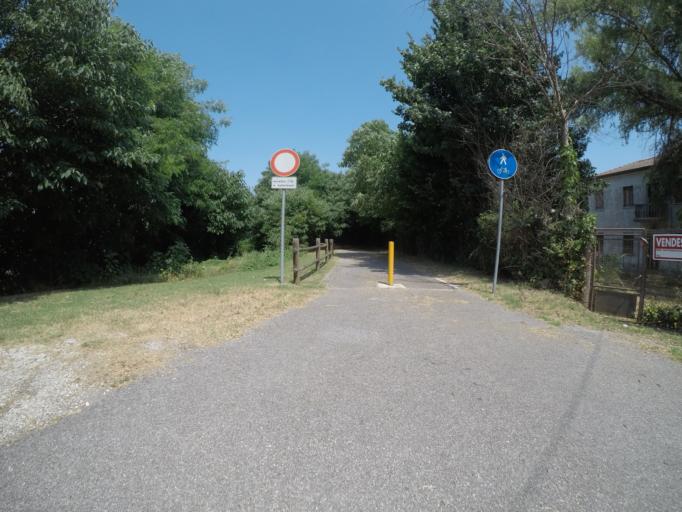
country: IT
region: Veneto
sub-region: Provincia di Rovigo
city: Villamarzana
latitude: 45.0054
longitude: 11.6819
